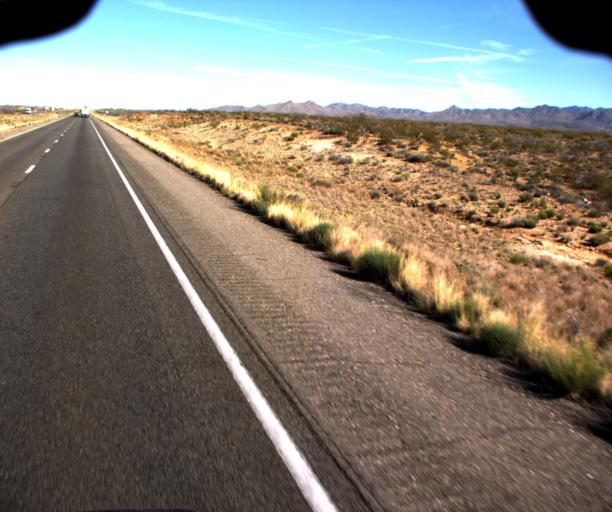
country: US
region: Arizona
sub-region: Mohave County
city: Golden Valley
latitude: 35.3511
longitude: -114.2260
